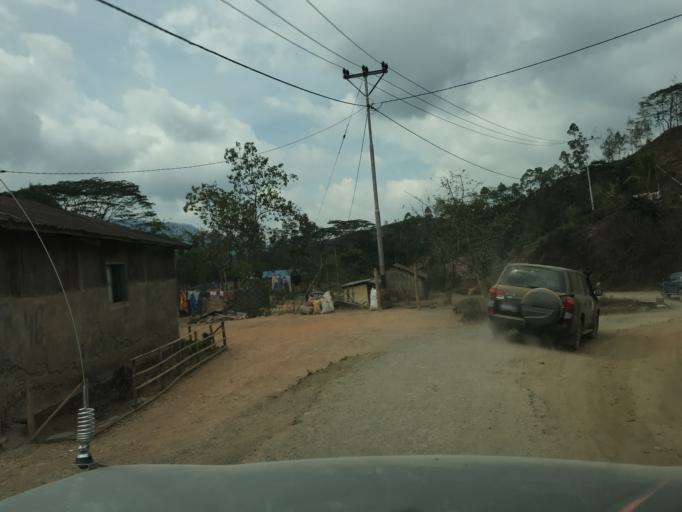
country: TL
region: Ermera
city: Gleno
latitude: -8.8212
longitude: 125.4321
